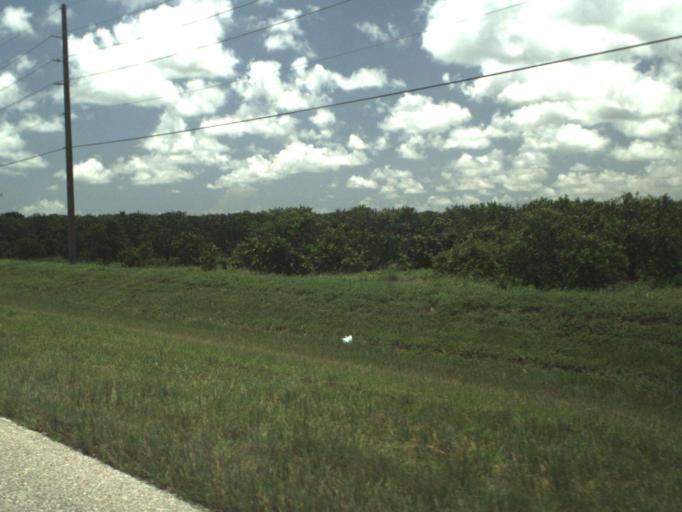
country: US
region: Florida
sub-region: Indian River County
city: West Vero Corridor
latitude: 27.6393
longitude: -80.5503
